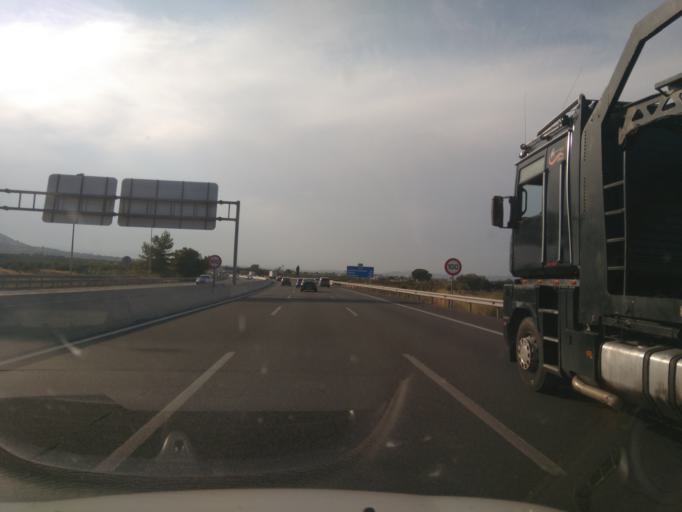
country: ES
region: Valencia
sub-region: Provincia de Valencia
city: Torrent
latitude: 39.4203
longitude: -0.5135
